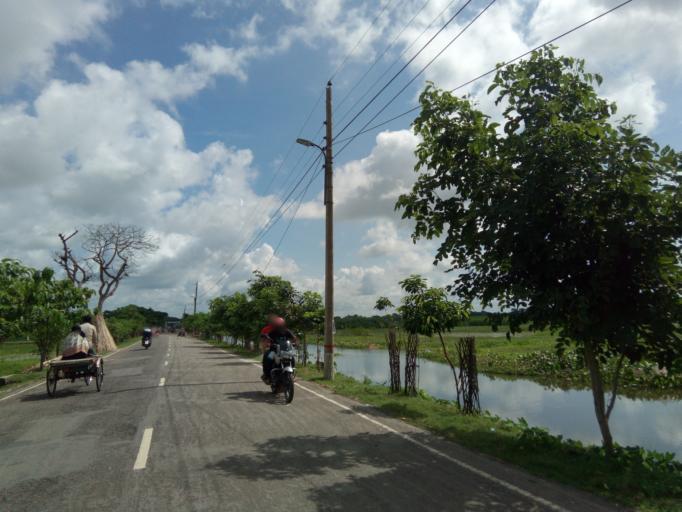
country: BD
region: Dhaka
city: Tungipara
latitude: 22.9005
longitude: 89.8967
